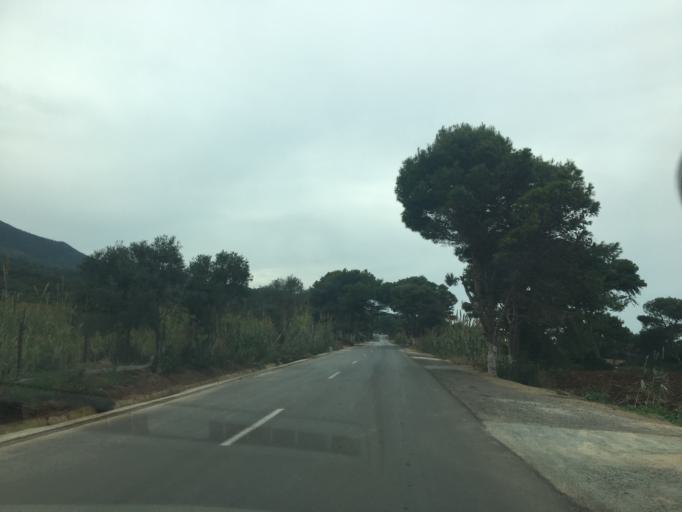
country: DZ
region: Tipaza
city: Tipasa
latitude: 36.6332
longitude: 2.3963
